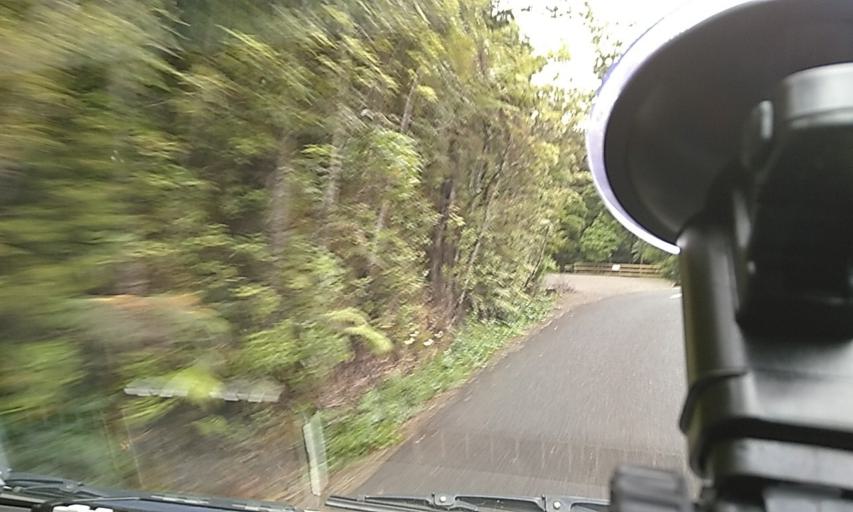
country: NZ
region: Northland
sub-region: Kaipara District
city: Dargaville
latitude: -35.6524
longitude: 173.5695
